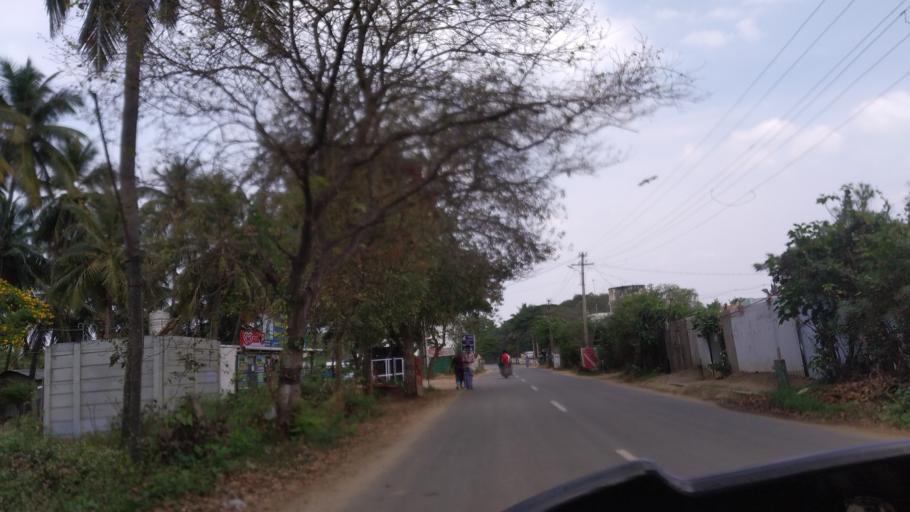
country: IN
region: Tamil Nadu
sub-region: Coimbatore
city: Perur
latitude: 10.9627
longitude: 76.7430
